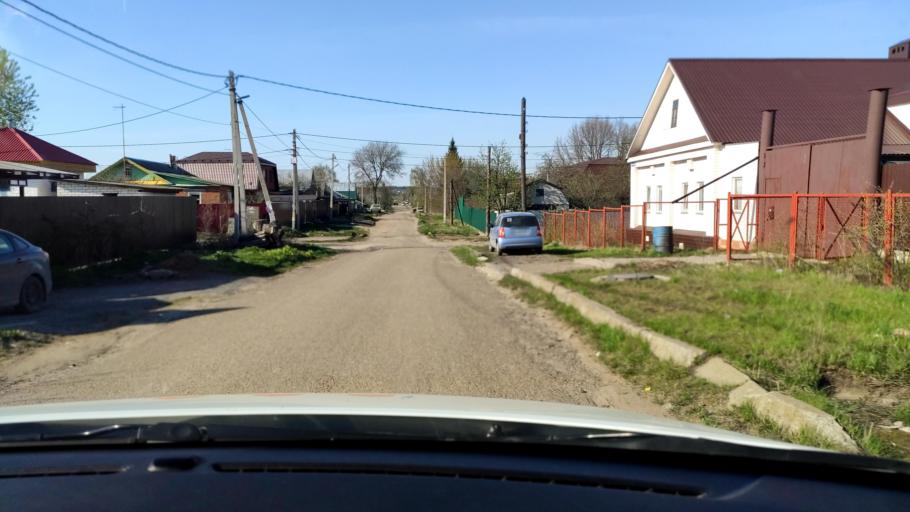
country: RU
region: Tatarstan
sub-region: Gorod Kazan'
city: Kazan
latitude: 55.8714
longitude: 49.0605
